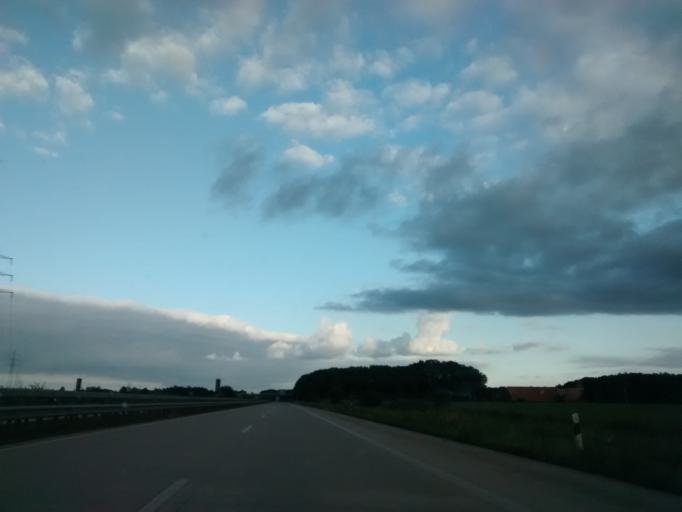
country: DE
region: Lower Saxony
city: Isterberg
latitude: 52.3365
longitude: 7.1222
